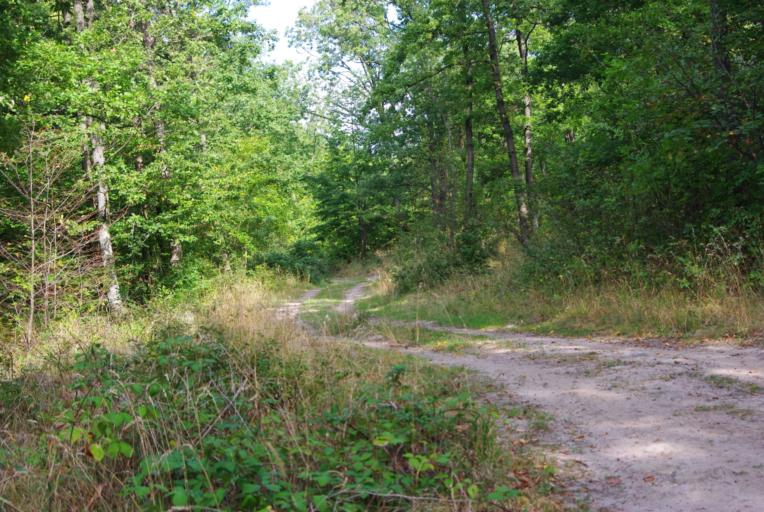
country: HU
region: Pest
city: Csobanka
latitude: 47.6820
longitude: 18.9601
